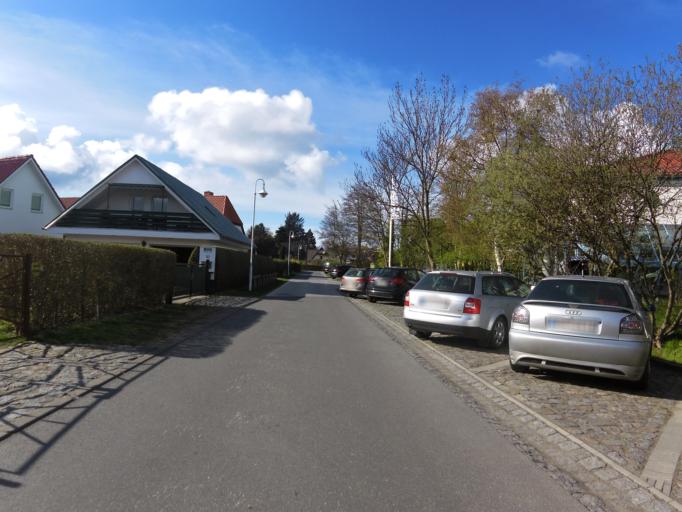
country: DE
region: Mecklenburg-Vorpommern
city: Zingst
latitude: 54.4377
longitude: 12.6929
